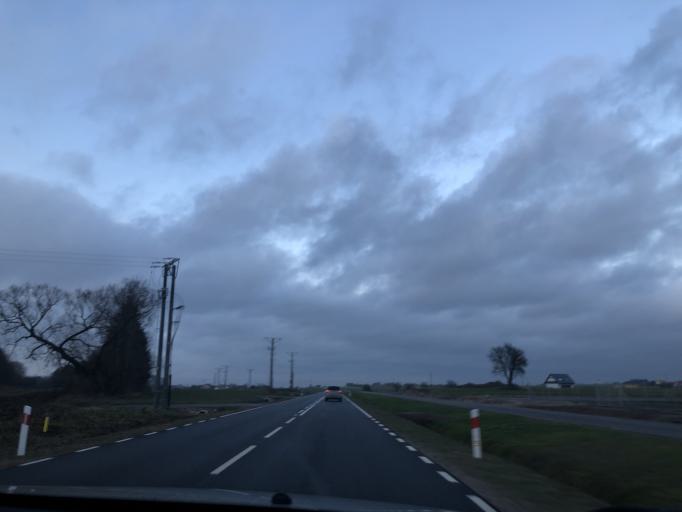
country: PL
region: Podlasie
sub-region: Lomza
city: Lomza
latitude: 53.1353
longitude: 22.0500
